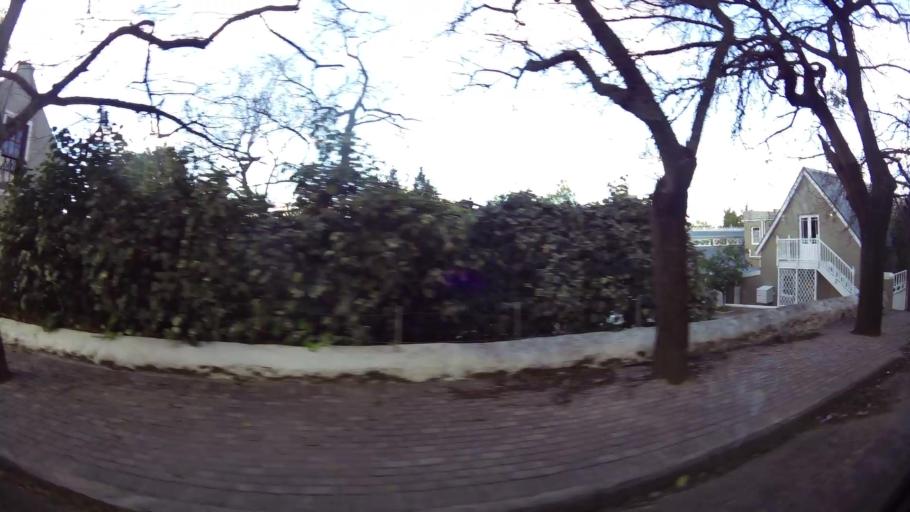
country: ZA
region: Western Cape
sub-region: Overberg District Municipality
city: Swellendam
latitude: -34.0159
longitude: 20.4496
